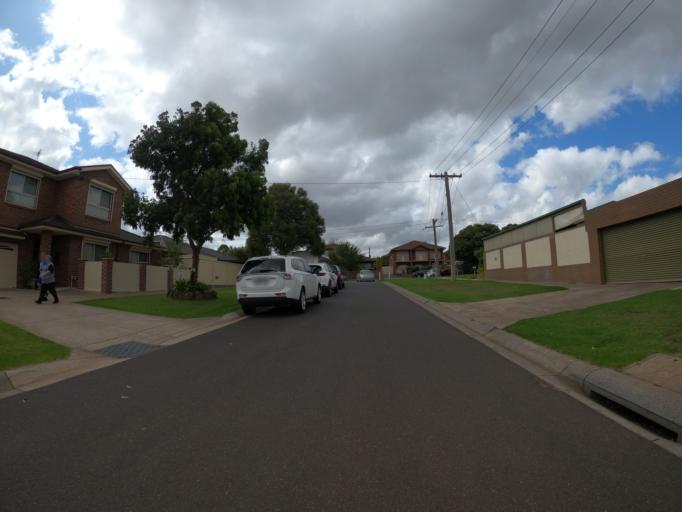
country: AU
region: Victoria
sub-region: Hume
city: Westmeadows
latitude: -37.6759
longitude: 144.8981
